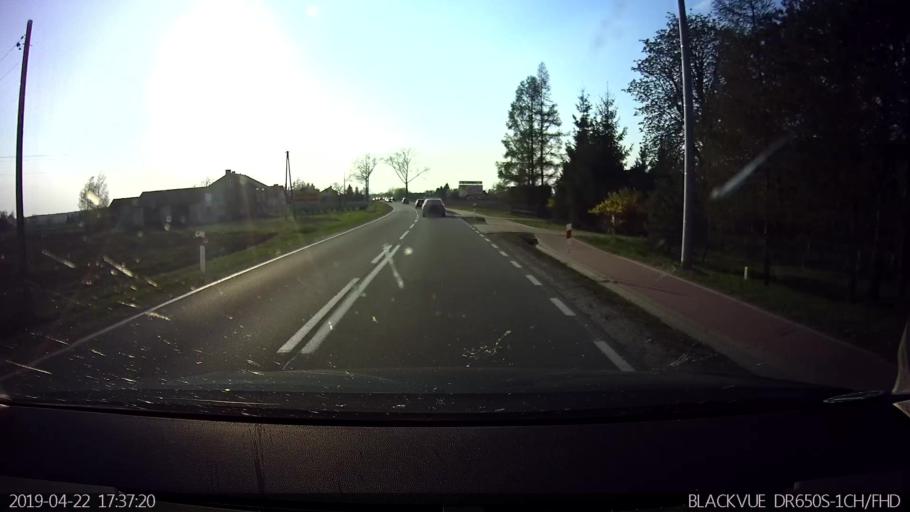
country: PL
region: Masovian Voivodeship
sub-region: Powiat sokolowski
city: Sokolow Podlaski
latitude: 52.4091
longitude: 22.1755
